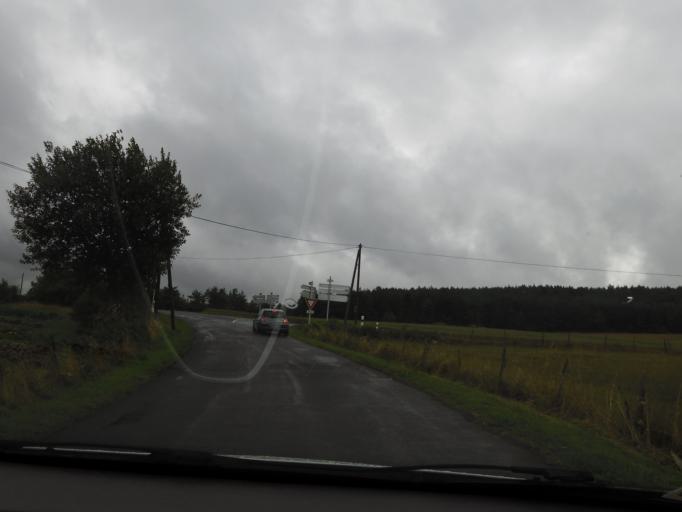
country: FR
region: Languedoc-Roussillon
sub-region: Departement de la Lozere
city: Mende
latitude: 44.4593
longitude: 3.4515
